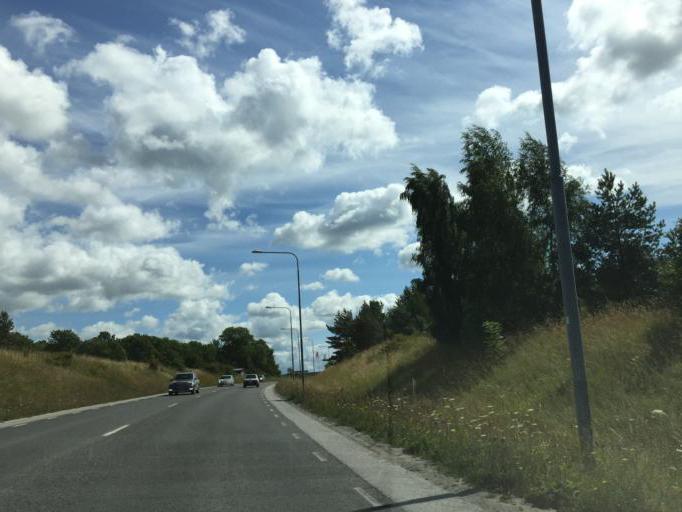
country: SE
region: Gotland
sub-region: Gotland
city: Visby
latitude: 57.6200
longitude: 18.2808
